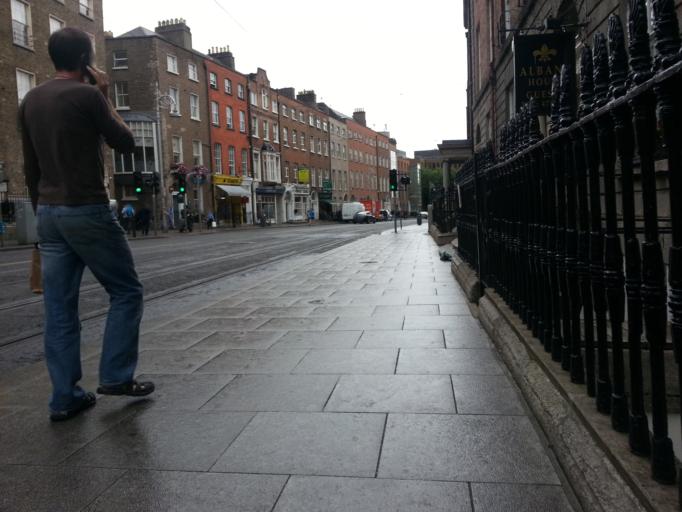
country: IE
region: Leinster
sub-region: Dublin City
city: Dublin
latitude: 53.3362
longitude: -6.2630
